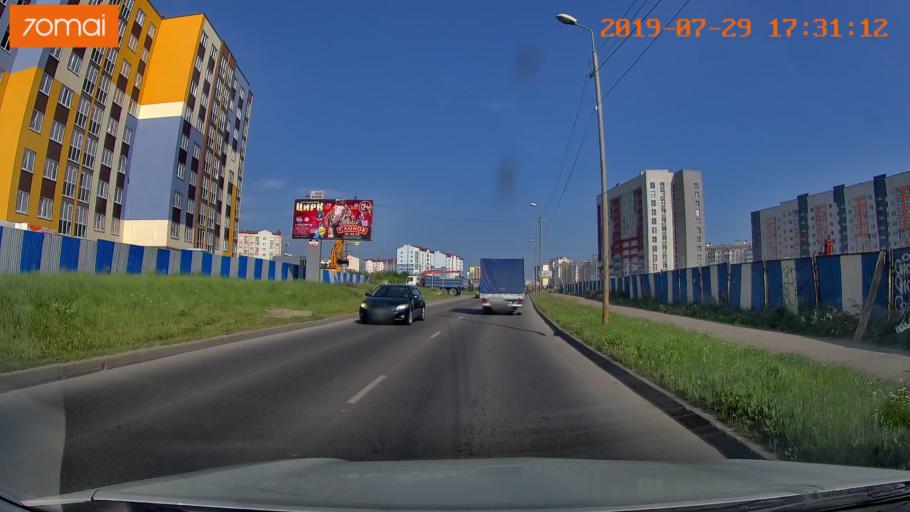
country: RU
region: Kaliningrad
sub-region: Gorod Kaliningrad
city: Kaliningrad
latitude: 54.7480
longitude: 20.4853
